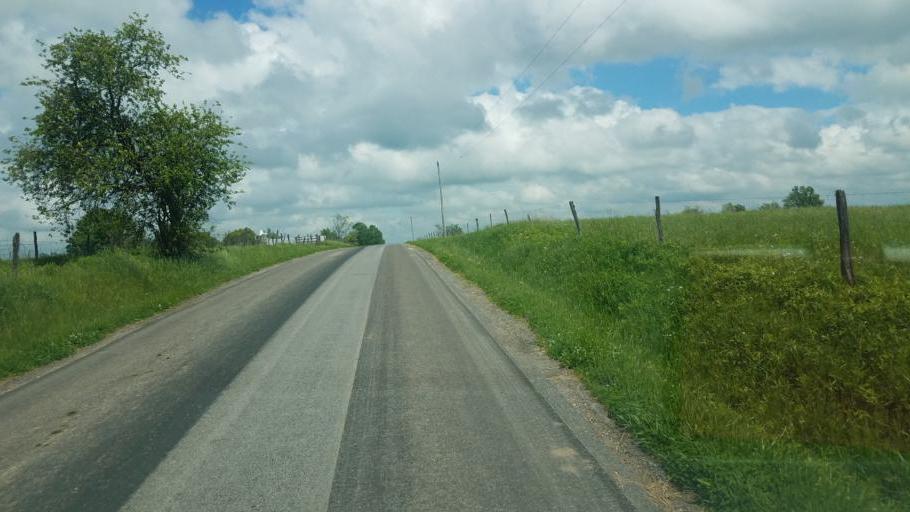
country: US
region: Ohio
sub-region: Wayne County
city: Apple Creek
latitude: 40.6753
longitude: -81.7697
